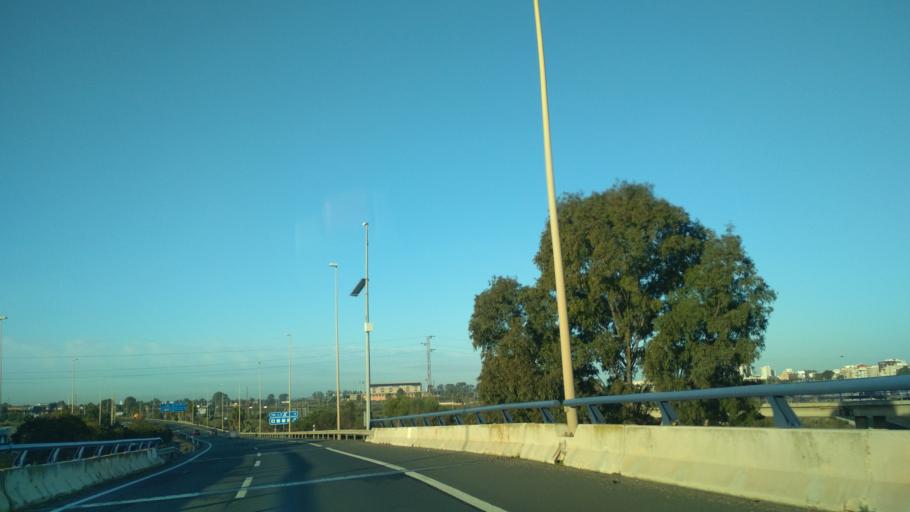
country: ES
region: Andalusia
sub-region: Provincia de Huelva
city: Huelva
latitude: 37.2513
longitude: -6.9362
